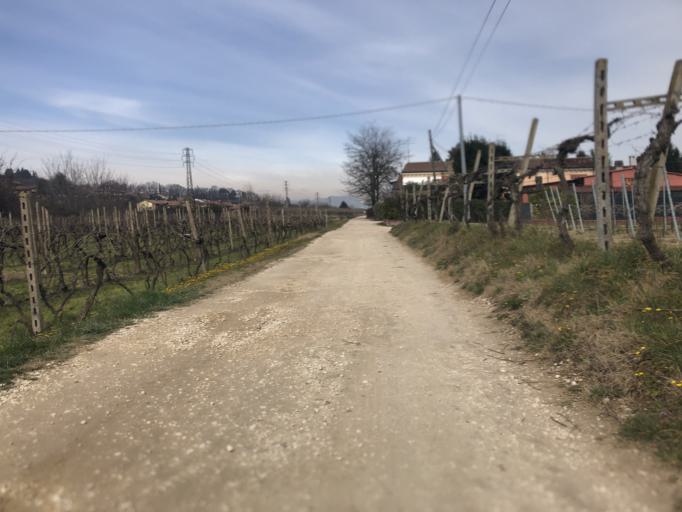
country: IT
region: Veneto
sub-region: Provincia di Verona
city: San Giorgio in Salici
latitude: 45.4268
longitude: 10.7941
